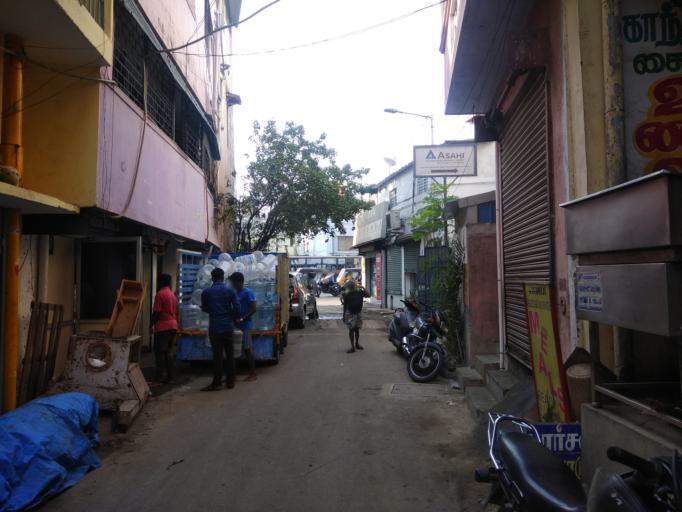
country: IN
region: Tamil Nadu
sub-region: Chennai
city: Gandhi Nagar
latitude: 13.0256
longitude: 80.2311
